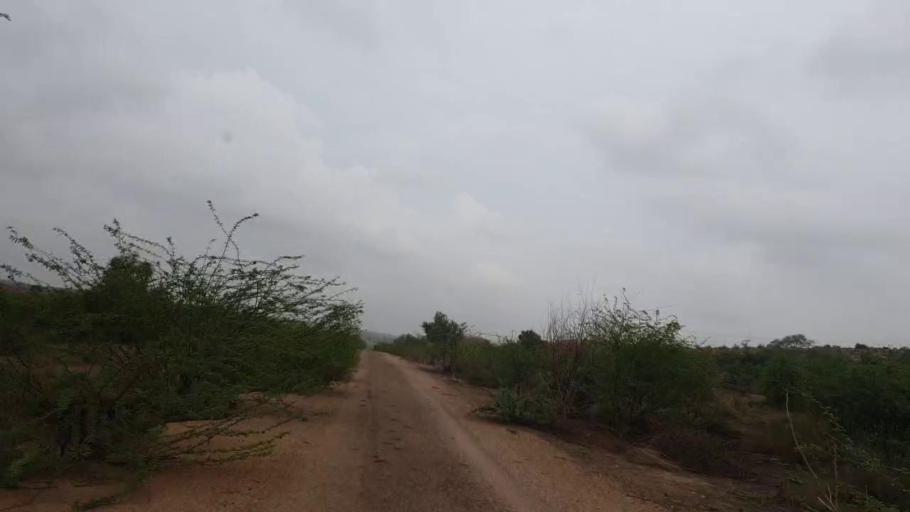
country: PK
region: Sindh
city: Diplo
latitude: 24.5139
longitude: 69.4774
